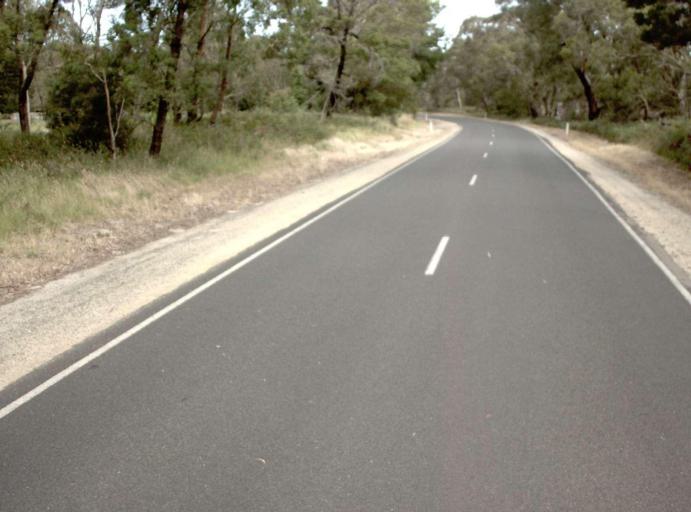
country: AU
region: Victoria
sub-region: Wellington
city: Sale
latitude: -38.2192
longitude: 147.1085
